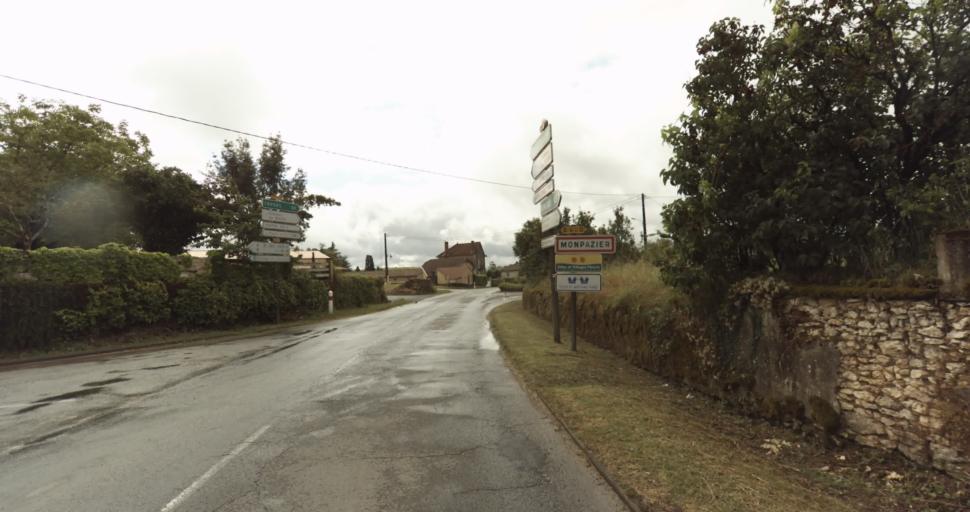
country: FR
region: Aquitaine
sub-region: Departement de la Dordogne
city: Belves
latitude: 44.6855
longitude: 0.8924
